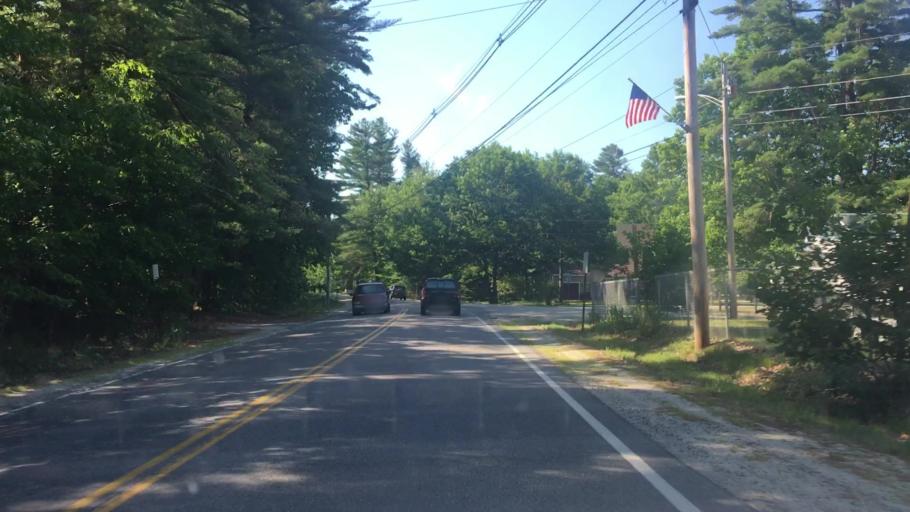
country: US
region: Maine
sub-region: York County
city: Hollis Center
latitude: 43.6835
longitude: -70.5874
